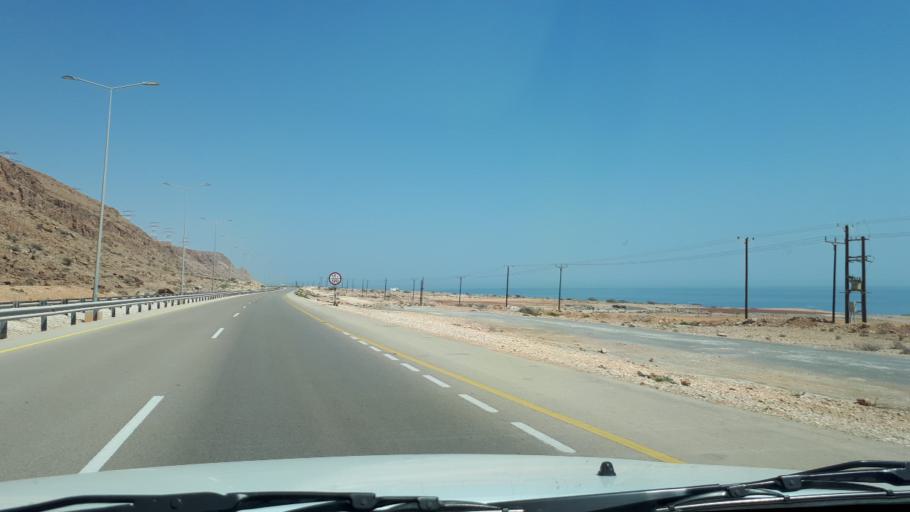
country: OM
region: Ash Sharqiyah
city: Sur
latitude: 22.7933
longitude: 59.2737
